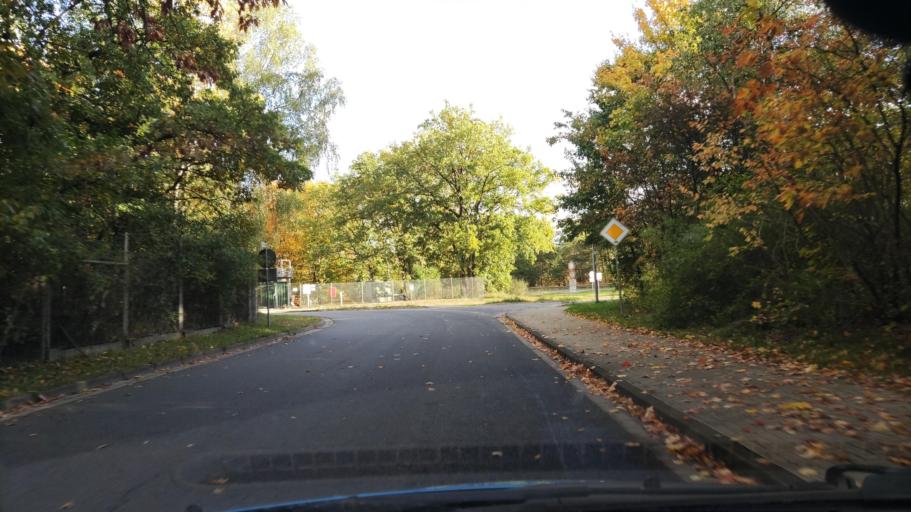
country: DE
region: Lower Saxony
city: Munster
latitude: 52.9745
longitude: 10.0823
